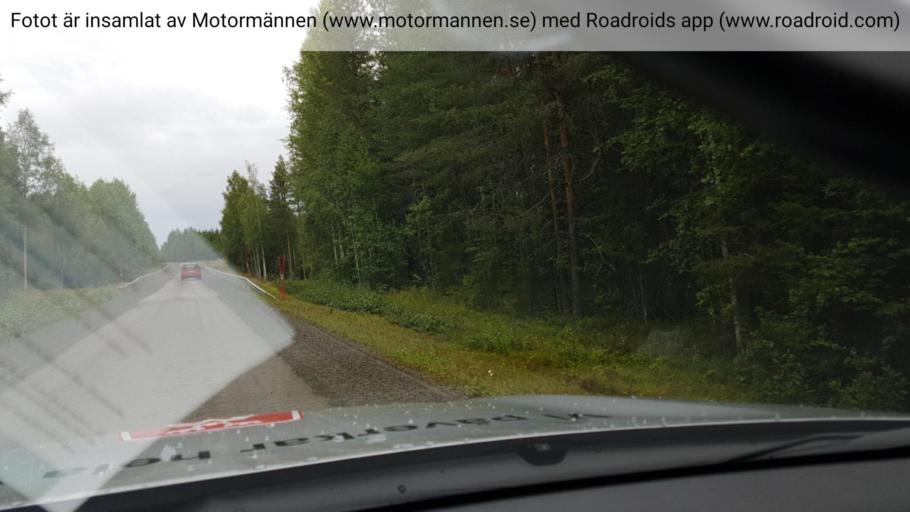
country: SE
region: Norrbotten
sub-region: Alvsbyns Kommun
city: AElvsbyn
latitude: 65.9693
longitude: 21.2191
